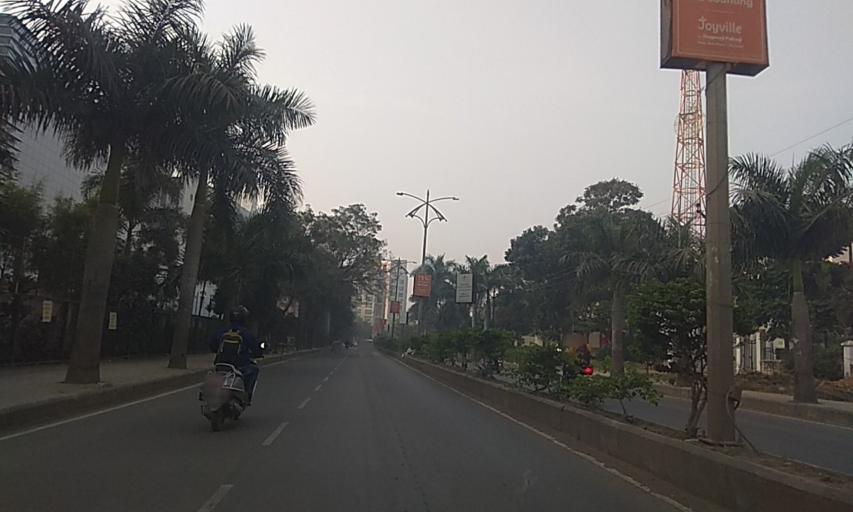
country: IN
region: Maharashtra
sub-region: Pune Division
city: Pimpri
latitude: 18.5886
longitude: 73.7377
